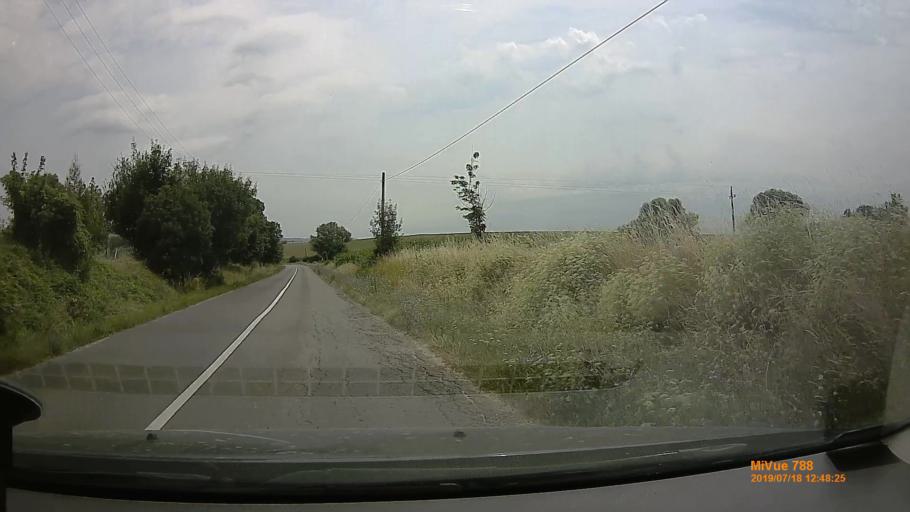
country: HU
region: Pest
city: Perbal
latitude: 47.5827
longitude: 18.7674
